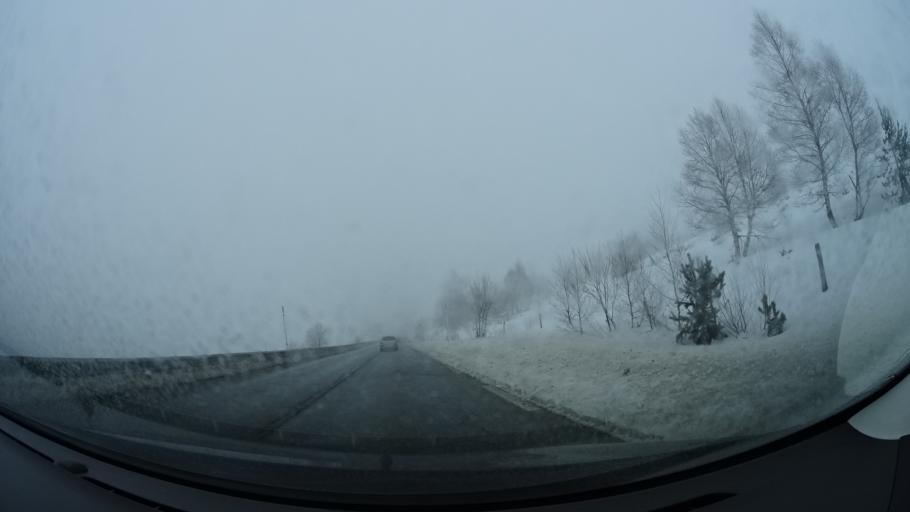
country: AD
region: Encamp
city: Pas de la Casa
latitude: 42.5659
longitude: 1.7783
